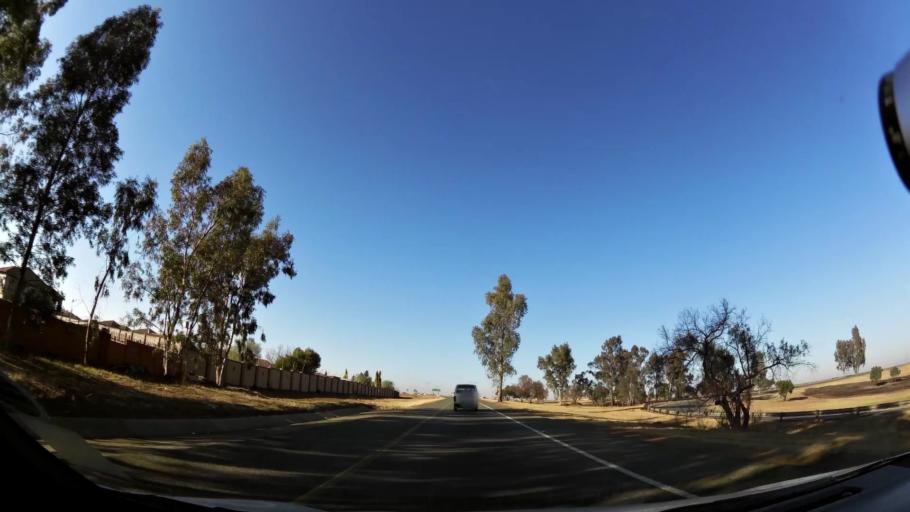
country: ZA
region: Gauteng
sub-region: Ekurhuleni Metropolitan Municipality
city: Germiston
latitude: -26.3506
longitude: 28.1026
